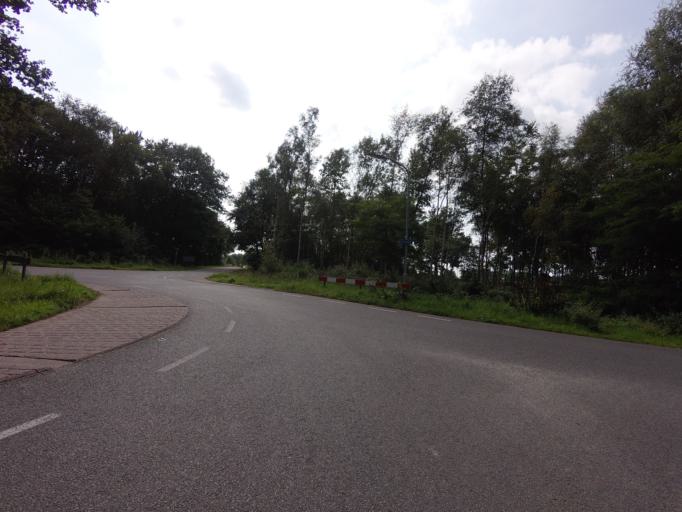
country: NL
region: Overijssel
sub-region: Gemeente Tubbergen
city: Tubbergen
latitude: 52.4137
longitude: 6.8333
